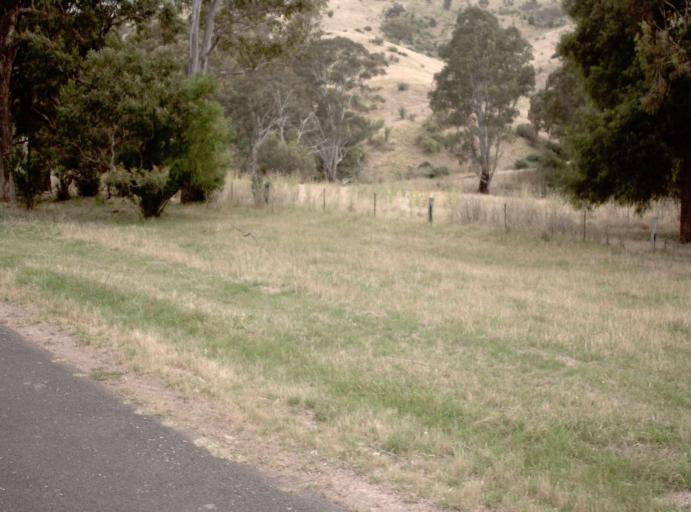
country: AU
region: Victoria
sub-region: Wellington
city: Heyfield
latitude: -37.6413
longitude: 146.6376
